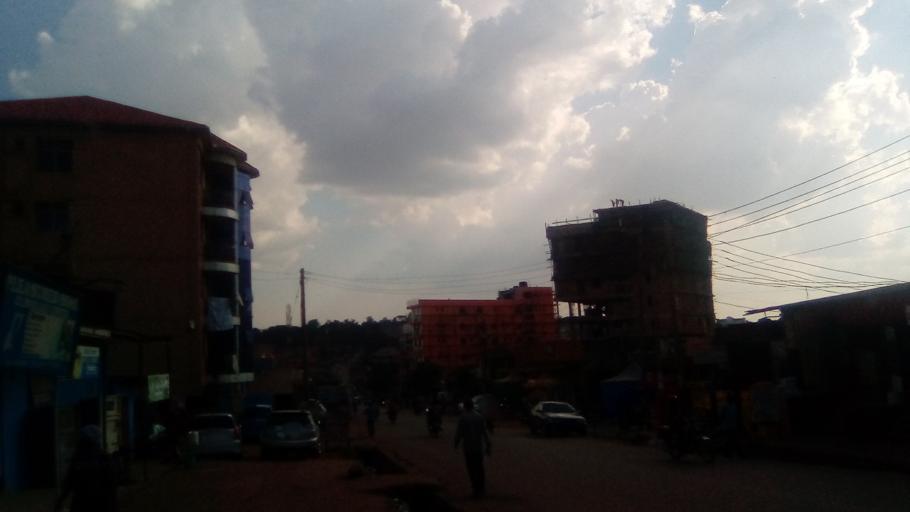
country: UG
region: Central Region
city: Kampala Central Division
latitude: 0.3123
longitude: 32.5675
